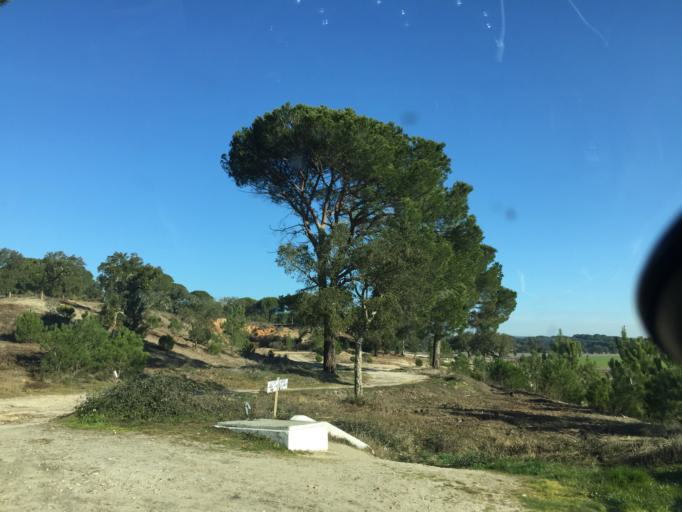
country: PT
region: Portalegre
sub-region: Ponte de Sor
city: Santo Andre
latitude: 39.0126
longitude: -8.2847
